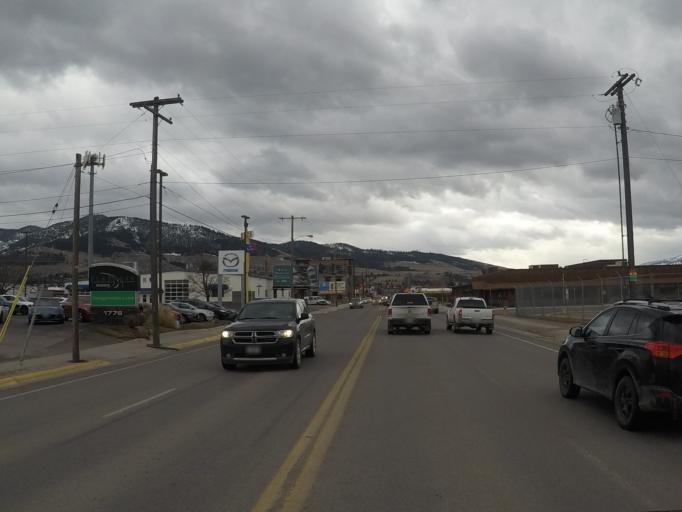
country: US
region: Montana
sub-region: Missoula County
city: Missoula
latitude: 46.8549
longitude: -114.0131
